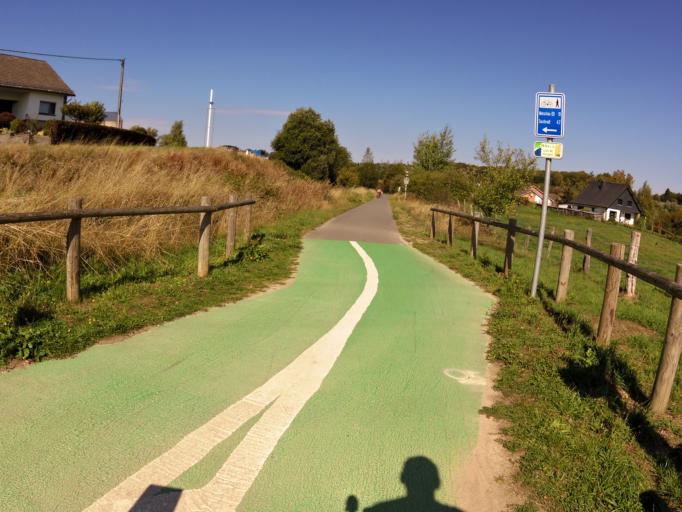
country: BE
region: Wallonia
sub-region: Province de Liege
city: Butgenbach
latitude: 50.4409
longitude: 6.1685
